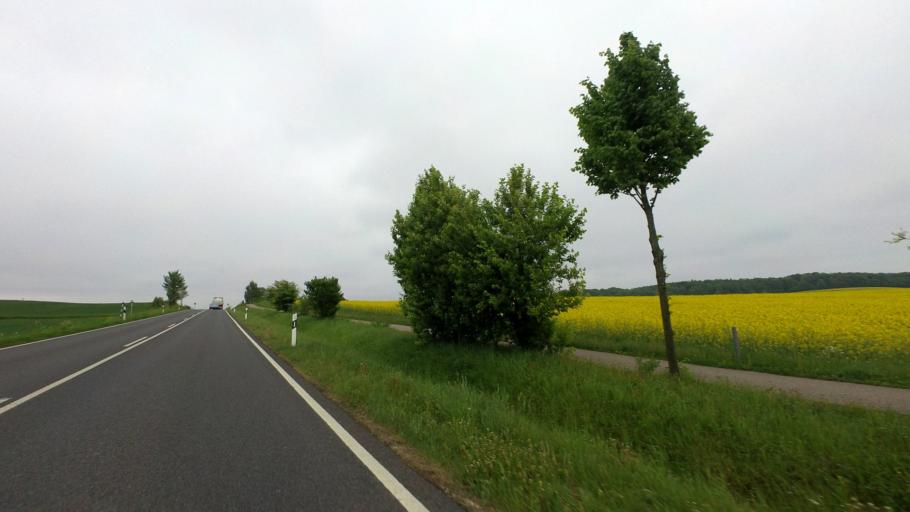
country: DE
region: Mecklenburg-Vorpommern
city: Wulkenzin
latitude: 53.5473
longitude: 13.1893
